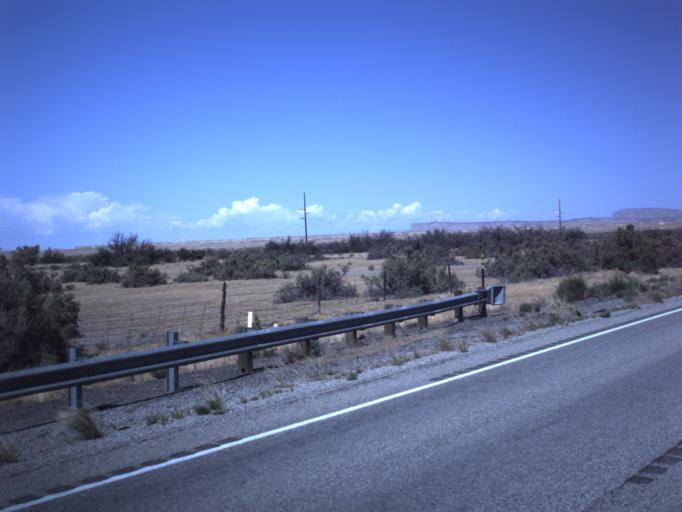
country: US
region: Utah
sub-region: Grand County
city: Moab
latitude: 38.8647
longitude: -109.8082
